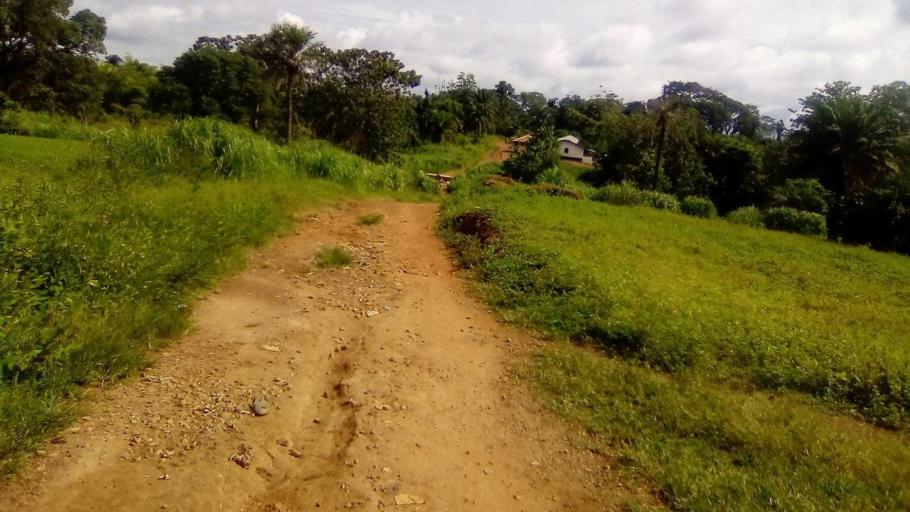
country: SL
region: Southern Province
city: Pujehun
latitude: 7.3722
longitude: -11.7277
